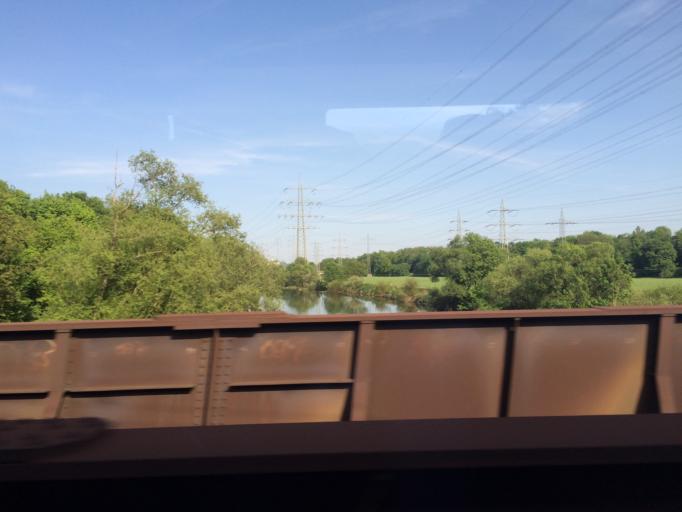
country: DE
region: North Rhine-Westphalia
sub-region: Regierungsbezirk Koln
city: Troisdorf
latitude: 50.7979
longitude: 7.1570
